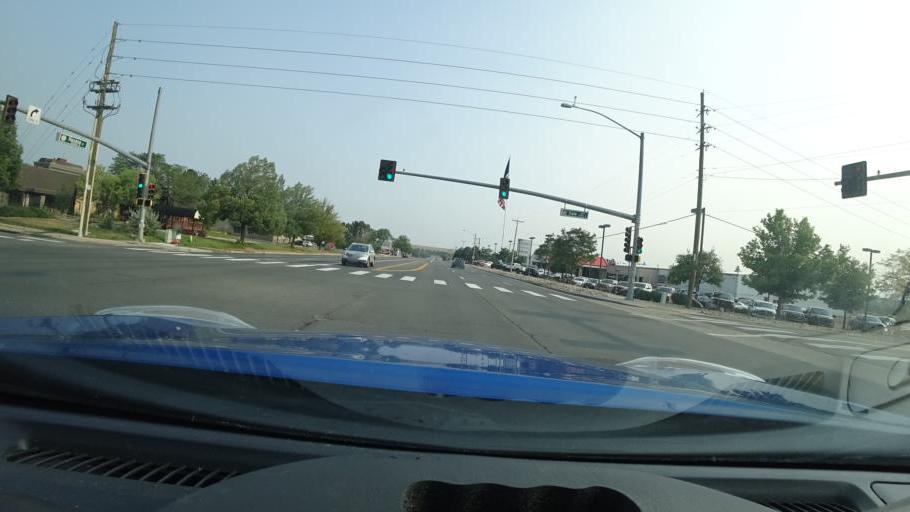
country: US
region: Colorado
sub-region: Adams County
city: Aurora
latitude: 39.6676
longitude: -104.8662
